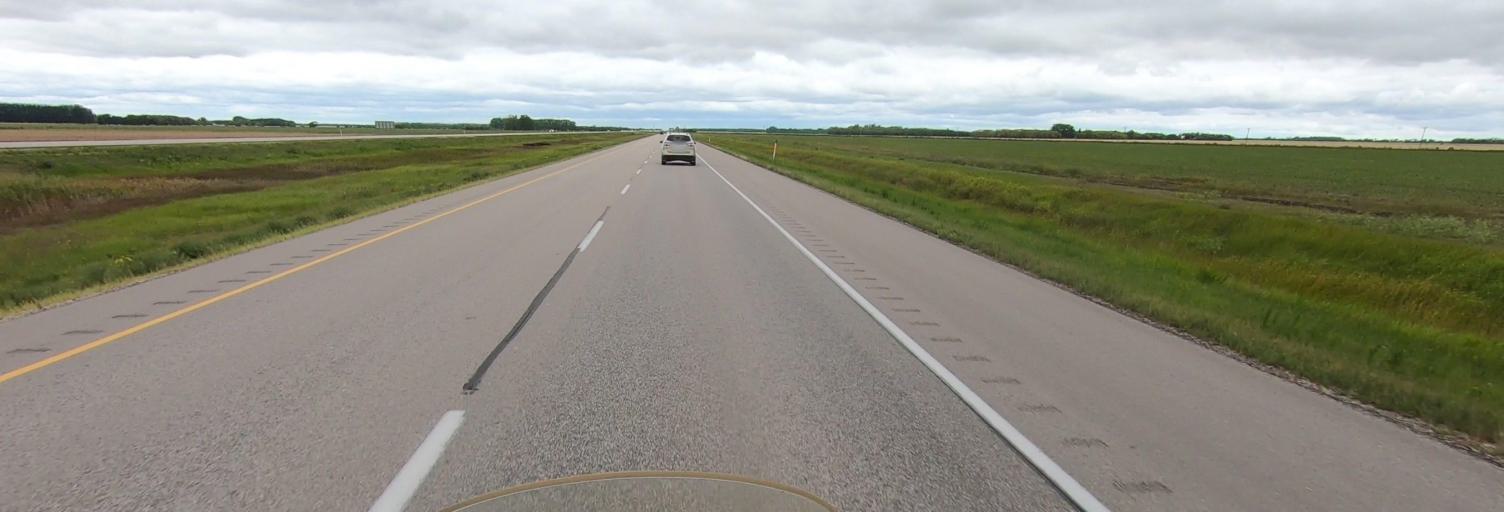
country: CA
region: Manitoba
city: Portage la Prairie
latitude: 49.9421
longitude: -97.9466
